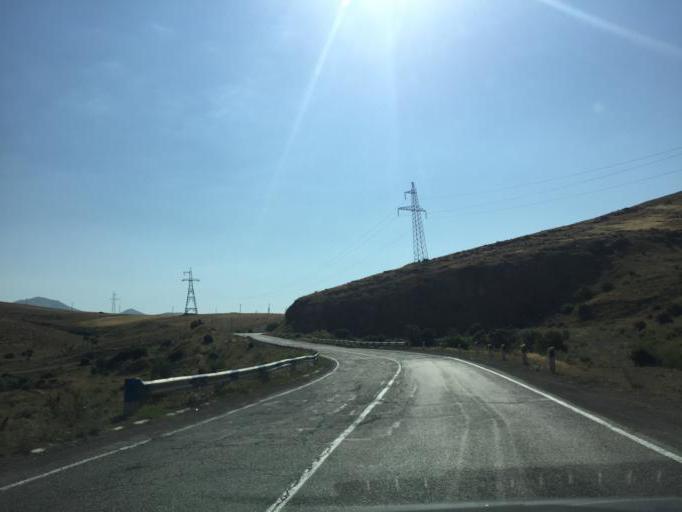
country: AM
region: Ararat
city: Zangakatun
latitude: 39.8169
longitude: 44.9834
